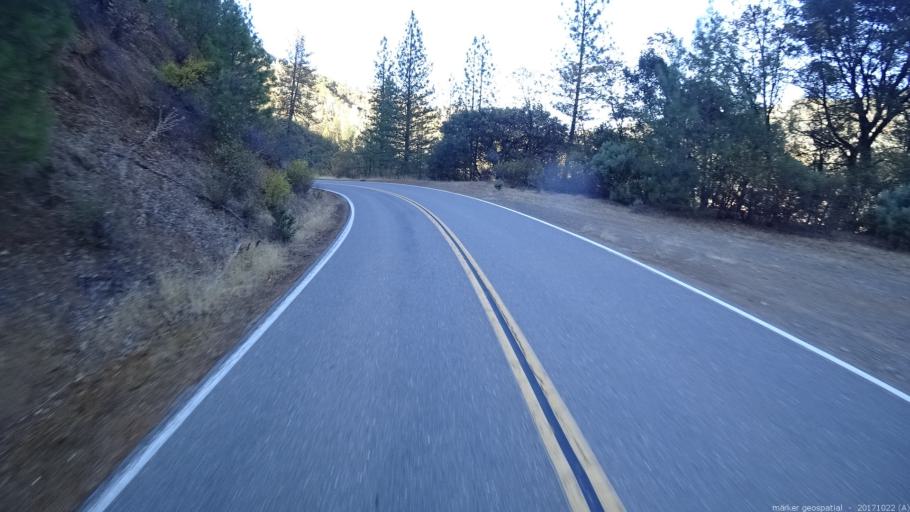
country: US
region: California
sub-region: Shasta County
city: Bella Vista
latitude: 40.8824
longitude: -122.2326
